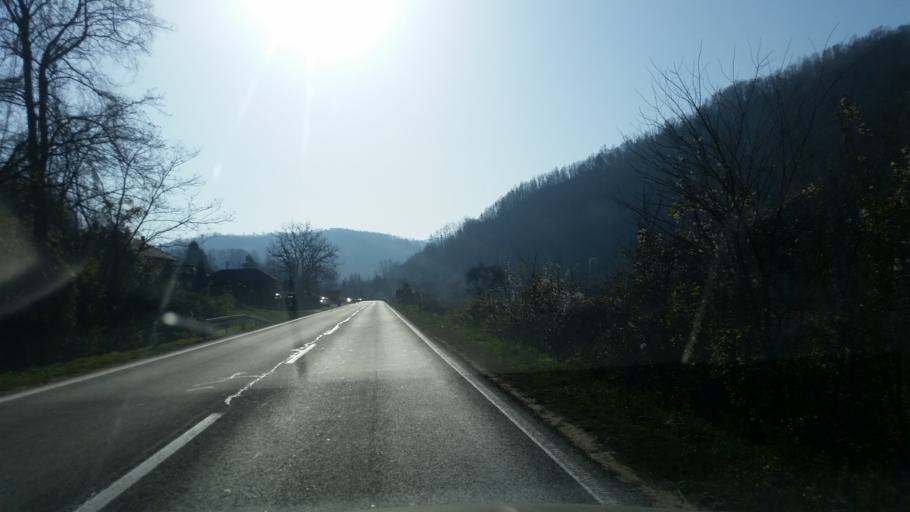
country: RS
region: Central Serbia
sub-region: Kolubarski Okrug
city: Ljig
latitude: 44.2063
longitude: 20.2256
